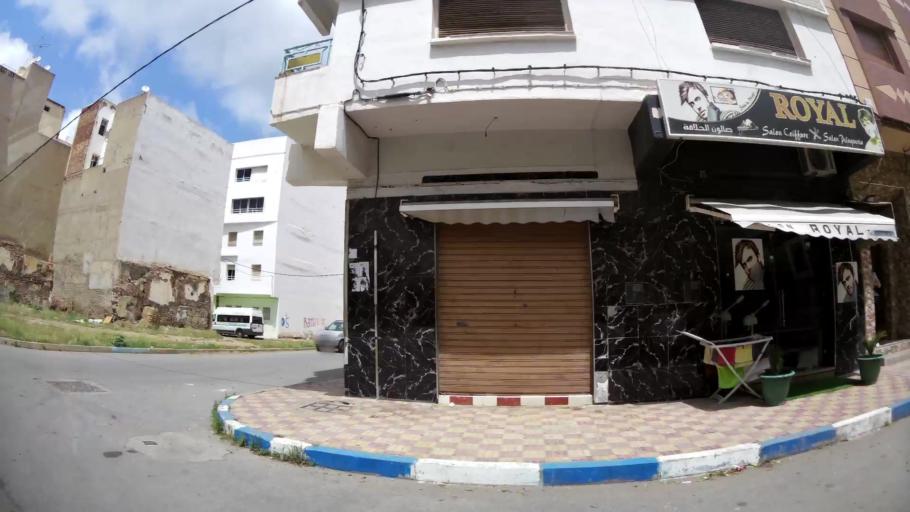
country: MA
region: Oriental
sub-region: Nador
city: Nador
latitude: 35.1819
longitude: -2.9260
